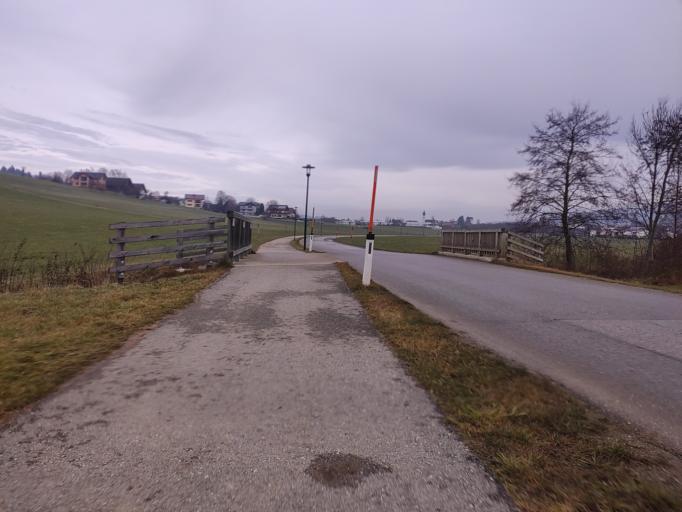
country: AT
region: Salzburg
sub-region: Politischer Bezirk Salzburg-Umgebung
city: Obertrum am See
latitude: 47.9265
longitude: 13.0739
